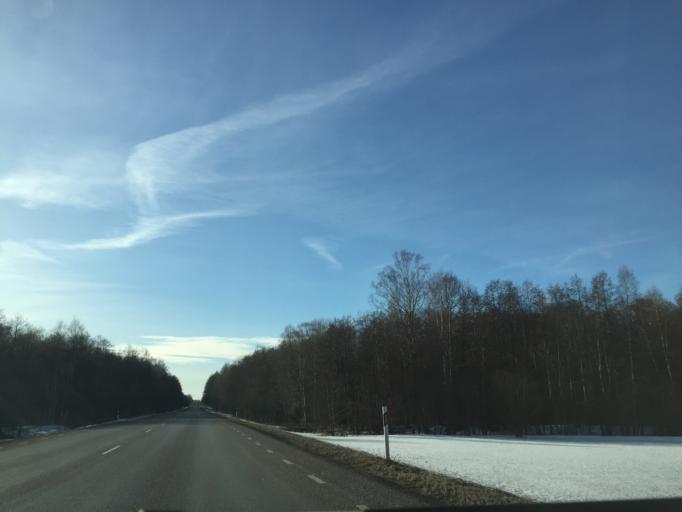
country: EE
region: Saare
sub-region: Orissaare vald
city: Orissaare
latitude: 58.5335
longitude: 23.0951
